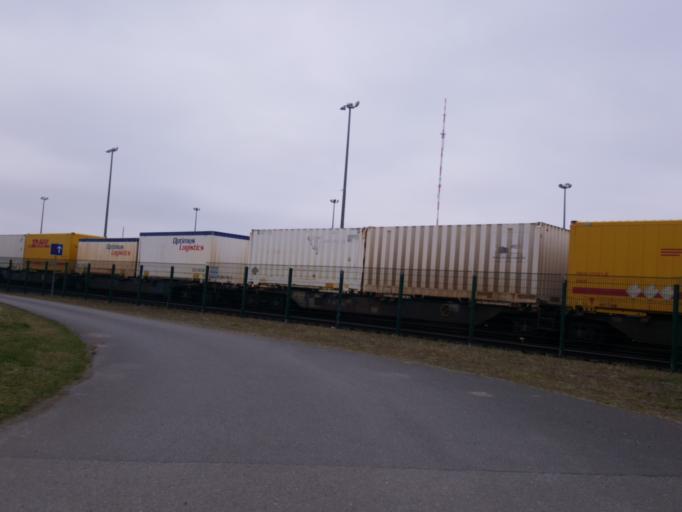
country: DE
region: Hamburg
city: Wandsbek
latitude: 53.5106
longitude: 10.1017
